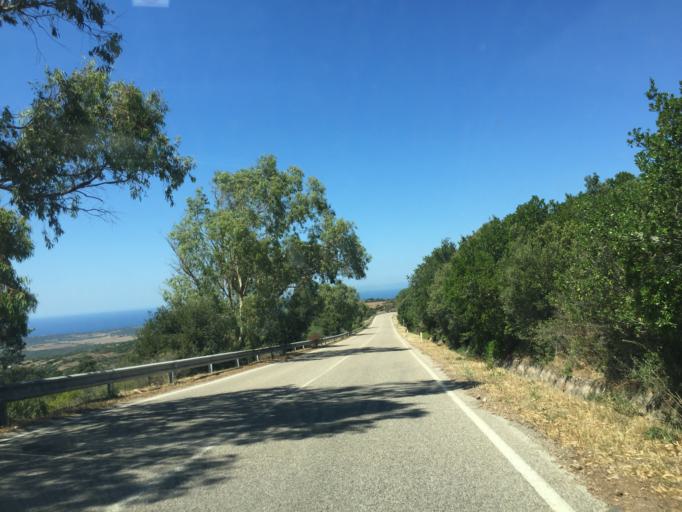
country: IT
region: Sardinia
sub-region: Provincia di Olbia-Tempio
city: Aglientu
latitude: 41.0908
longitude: 9.0976
